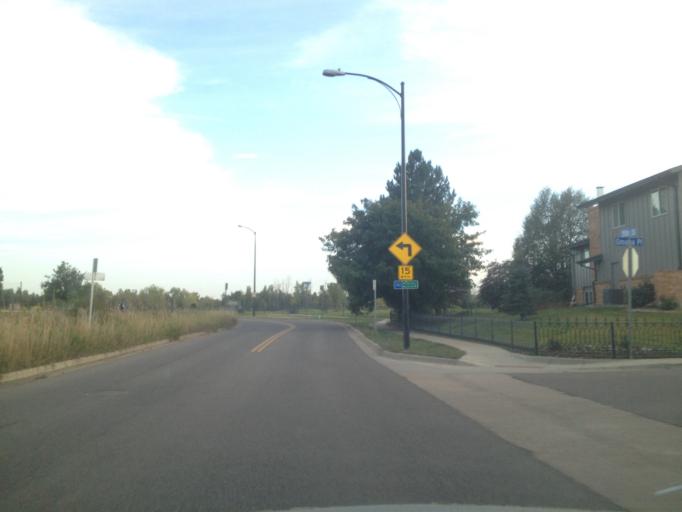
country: US
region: Colorado
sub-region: Boulder County
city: Boulder
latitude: 39.9936
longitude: -105.2244
